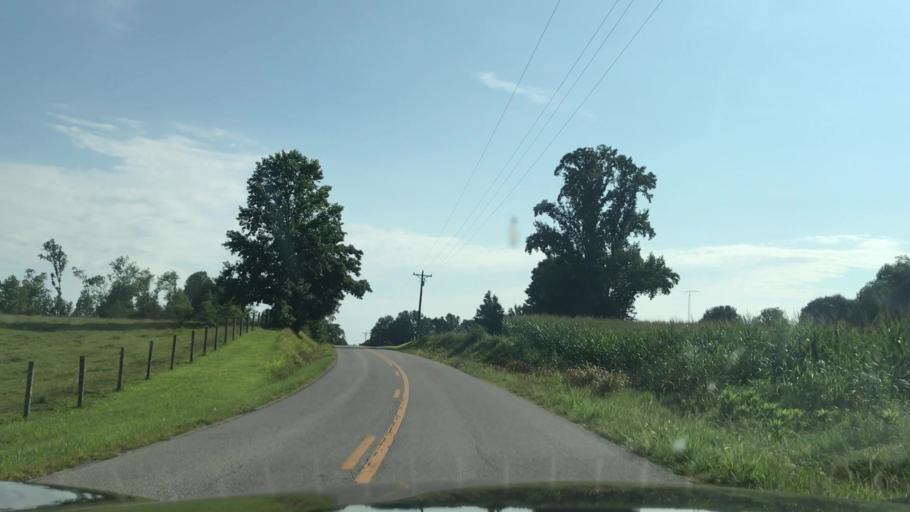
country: US
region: Kentucky
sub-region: Hart County
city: Horse Cave
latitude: 37.1896
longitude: -85.7622
